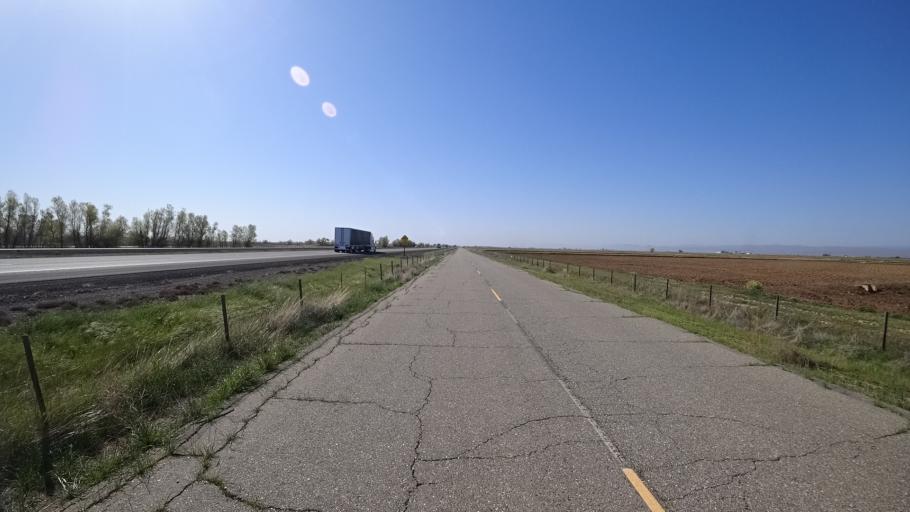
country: US
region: California
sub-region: Glenn County
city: Willows
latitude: 39.4323
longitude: -122.1938
